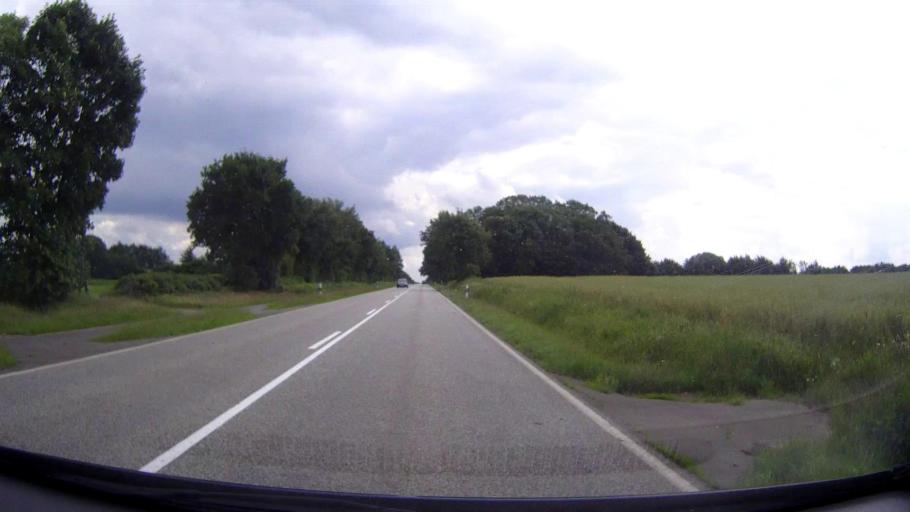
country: DE
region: Schleswig-Holstein
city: Warringholz
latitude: 54.0890
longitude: 9.4656
